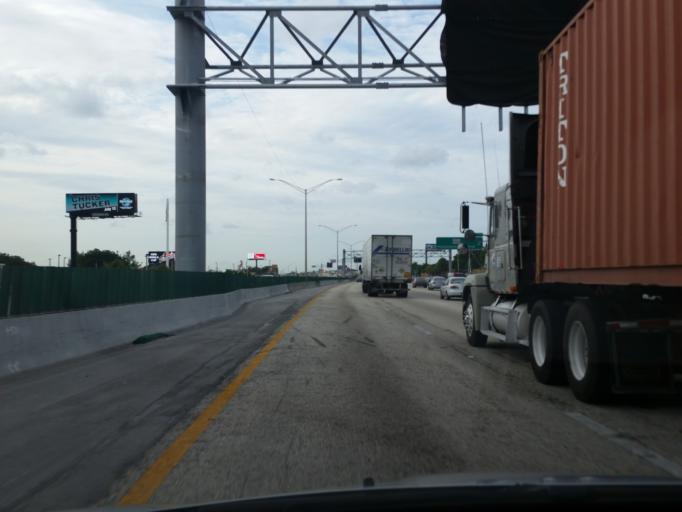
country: US
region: Florida
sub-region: Broward County
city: Pembroke Park
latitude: 25.9783
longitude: -80.1660
